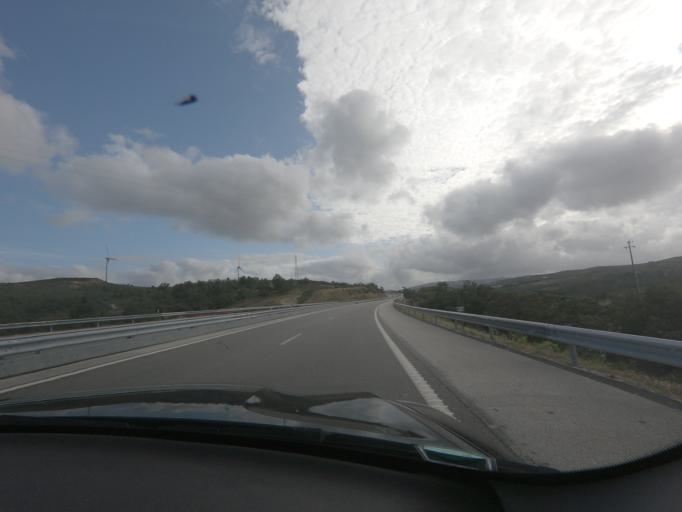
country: PT
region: Viseu
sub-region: Tarouca
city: Tarouca
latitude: 41.0209
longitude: -7.8767
